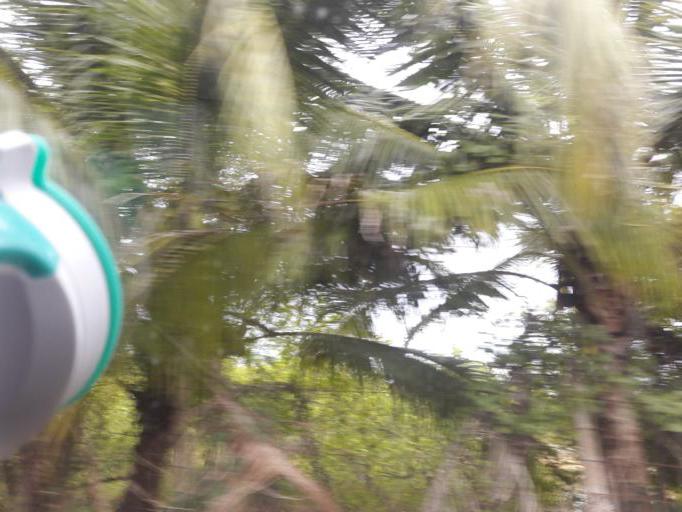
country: TH
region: Ratchaburi
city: Damnoen Saduak
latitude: 13.5267
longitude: 100.0081
